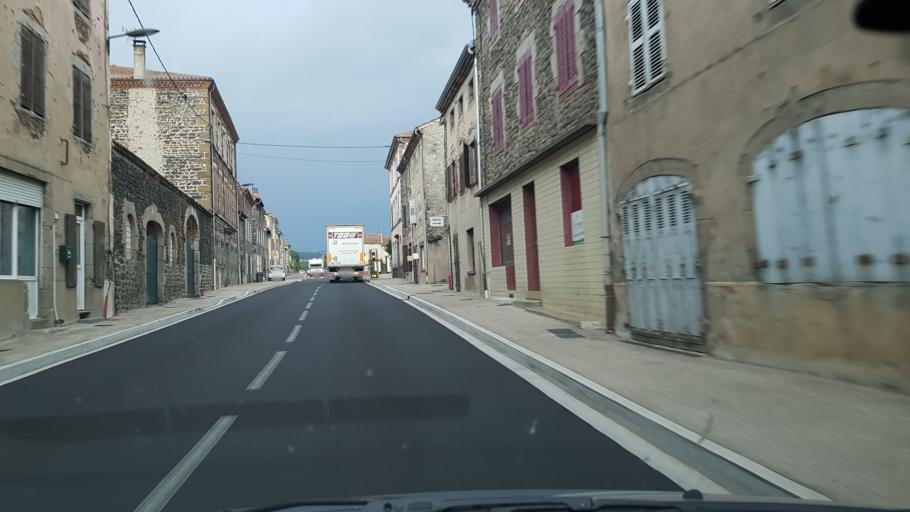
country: FR
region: Auvergne
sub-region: Departement de la Haute-Loire
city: Paulhaguet
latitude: 45.1562
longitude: 3.5410
